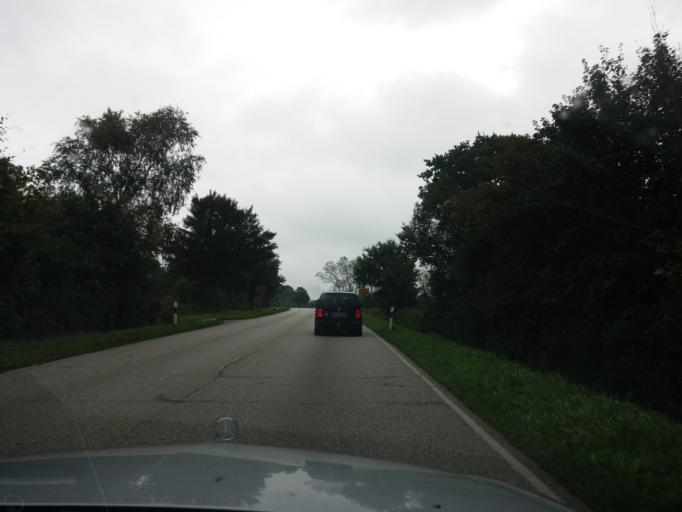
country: DE
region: Schleswig-Holstein
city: Treia
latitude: 54.5157
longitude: 9.3307
